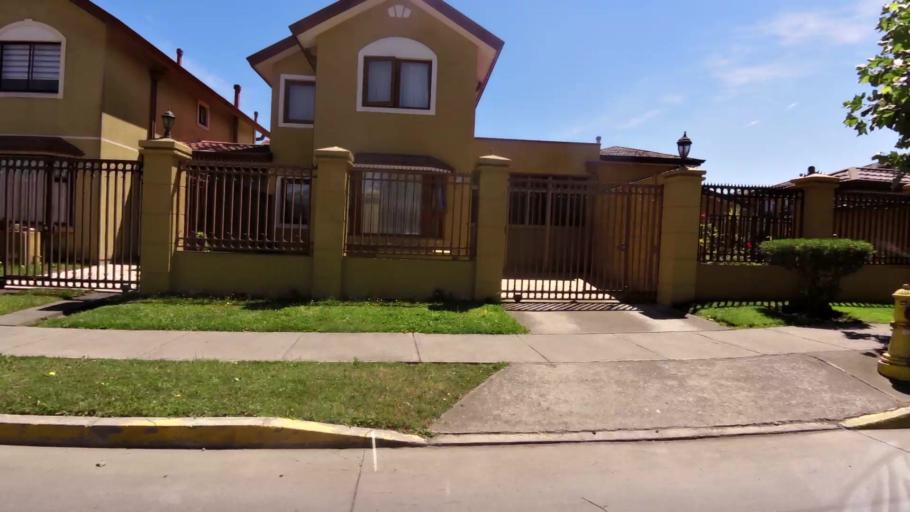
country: CL
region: Biobio
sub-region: Provincia de Concepcion
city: Talcahuano
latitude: -36.7553
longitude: -73.0870
